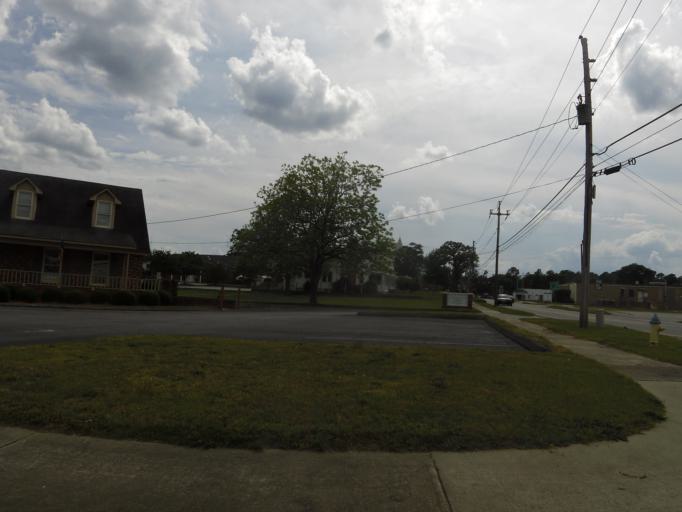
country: US
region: Georgia
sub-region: McDuffie County
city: Thomson
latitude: 33.4712
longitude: -82.5030
